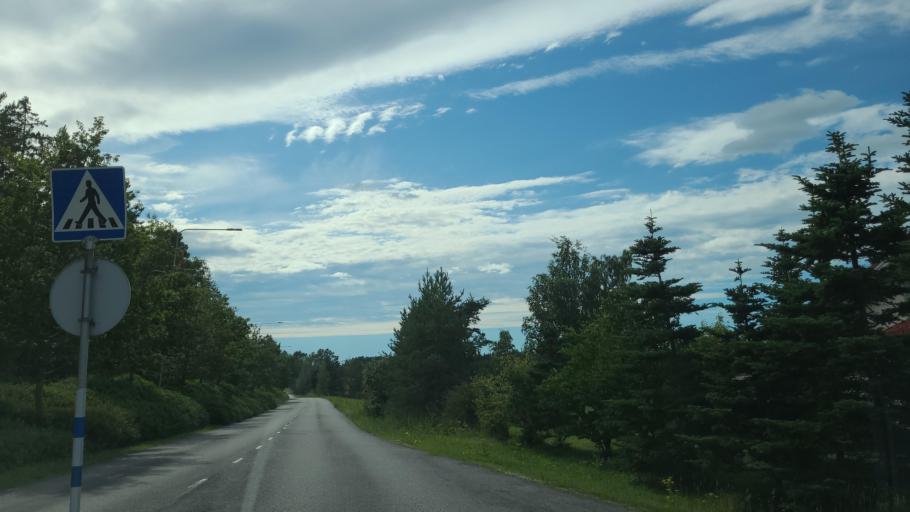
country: FI
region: Varsinais-Suomi
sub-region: Turku
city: Naantali
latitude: 60.4625
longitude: 21.9917
